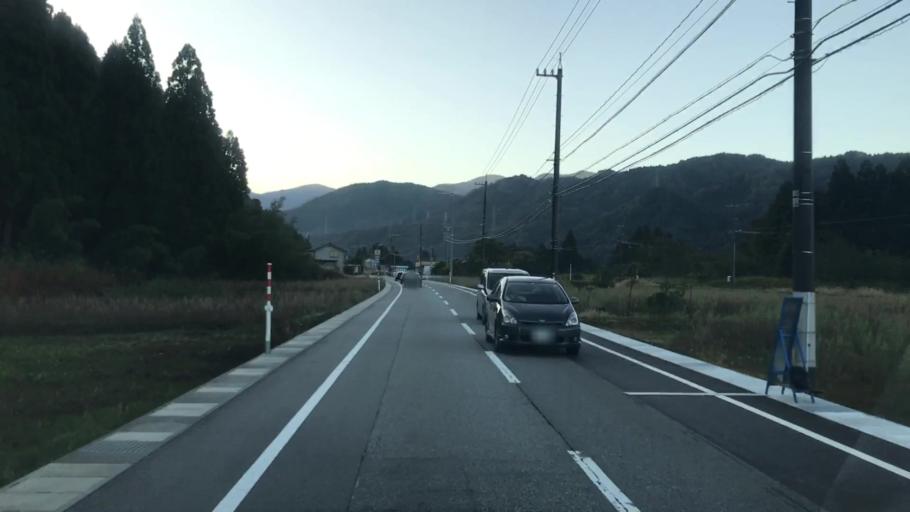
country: JP
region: Toyama
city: Kamiichi
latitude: 36.5866
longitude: 137.3325
